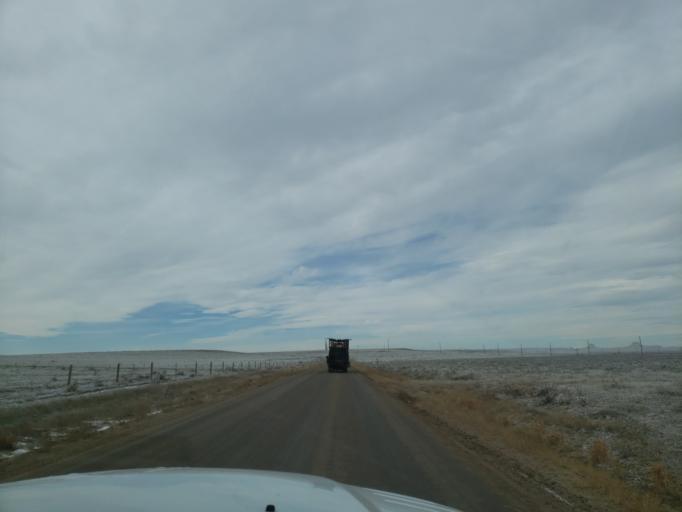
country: US
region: Wyoming
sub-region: Laramie County
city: Pine Bluffs
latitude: 40.7877
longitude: -103.8824
